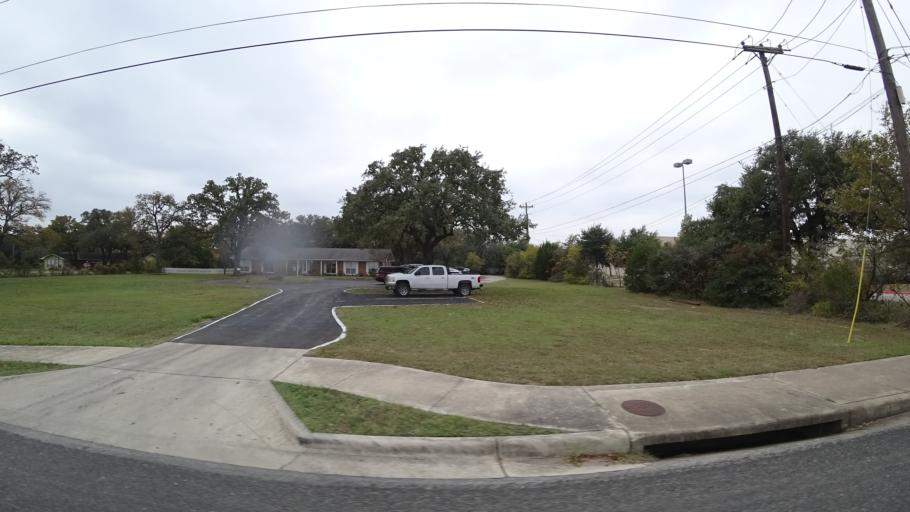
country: US
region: Texas
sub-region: Williamson County
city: Anderson Mill
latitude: 30.4540
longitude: -97.8238
